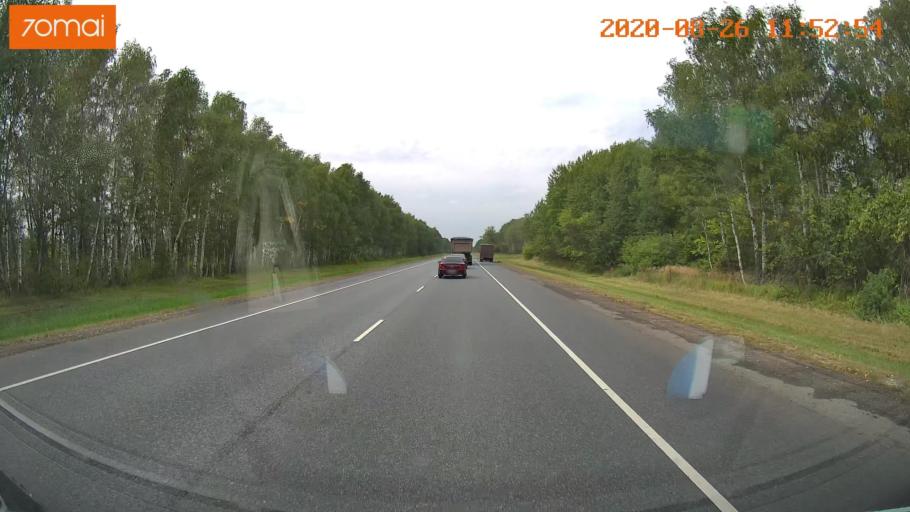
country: RU
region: Rjazan
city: Lesnoy
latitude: 54.2925
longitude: 40.4421
